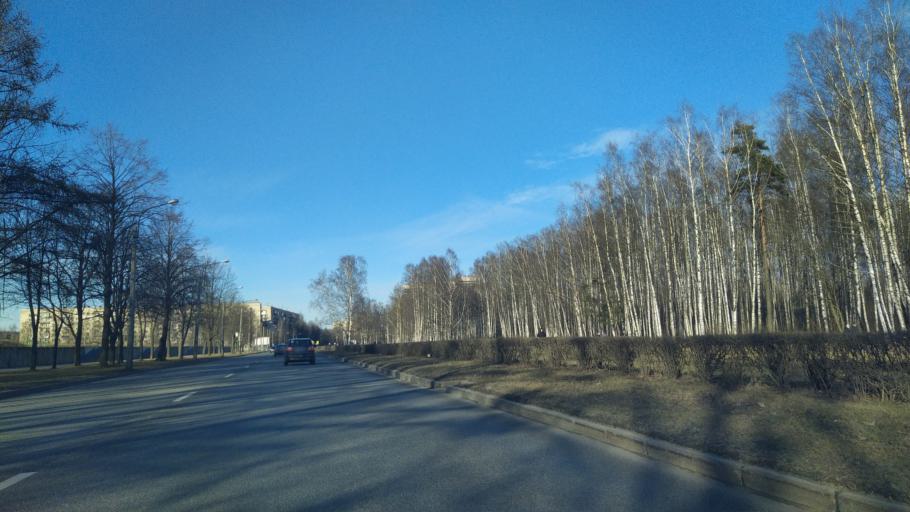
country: RU
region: Leningrad
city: Kalininskiy
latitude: 59.9967
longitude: 30.3926
